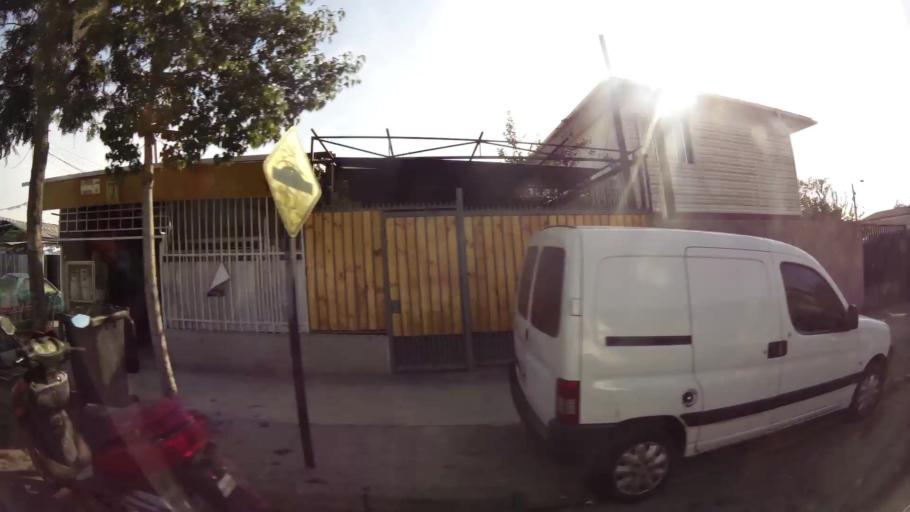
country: CL
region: Santiago Metropolitan
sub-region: Provincia de Santiago
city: Santiago
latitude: -33.5109
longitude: -70.6319
